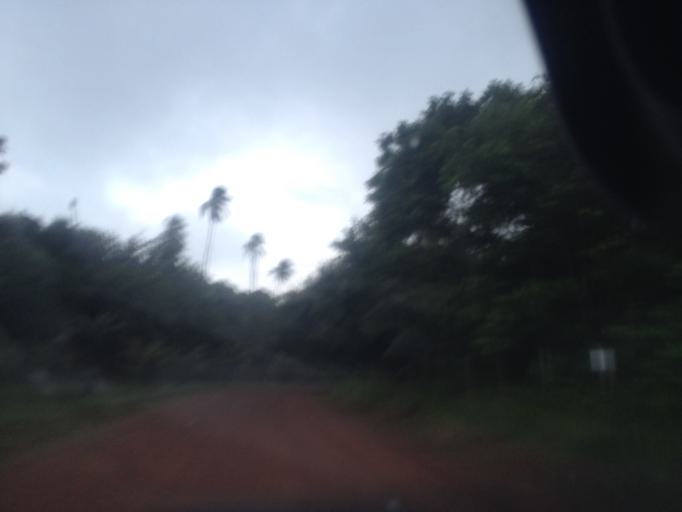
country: BR
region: Bahia
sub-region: Mata De Sao Joao
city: Mata de Sao Joao
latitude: -12.5783
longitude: -38.0308
